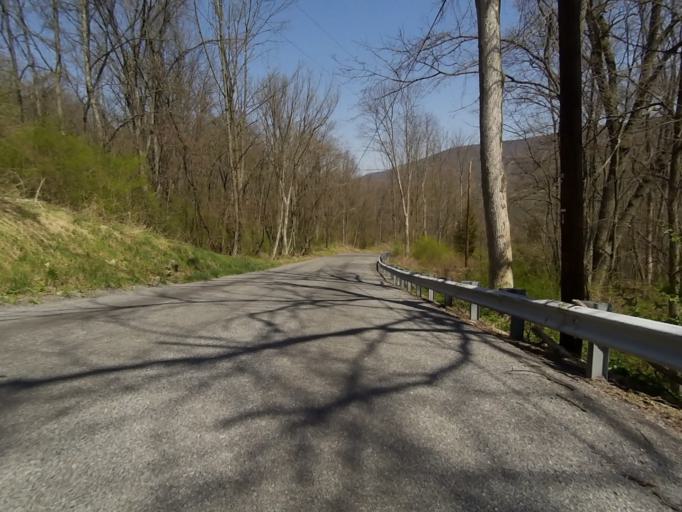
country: US
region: Pennsylvania
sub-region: Blair County
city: Williamsburg
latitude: 40.5132
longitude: -78.1728
